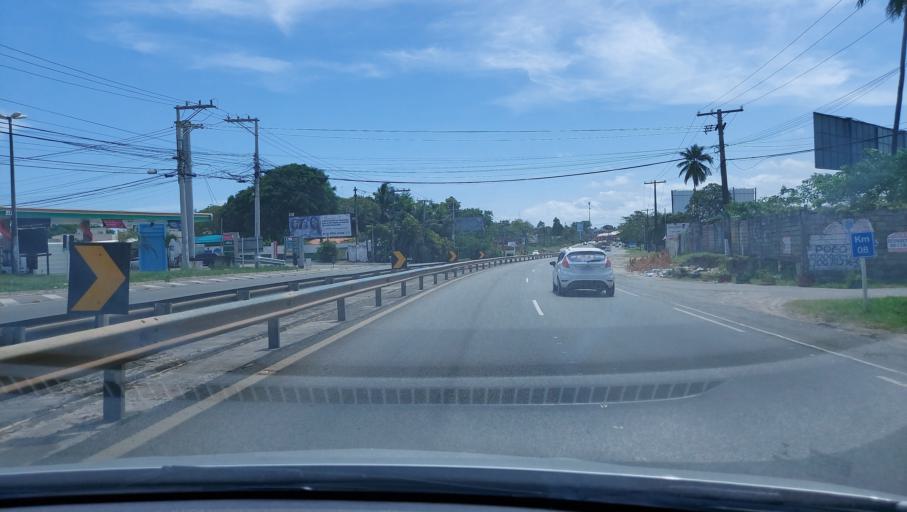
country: BR
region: Bahia
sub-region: Lauro De Freitas
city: Lauro de Freitas
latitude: -12.8599
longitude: -38.2882
